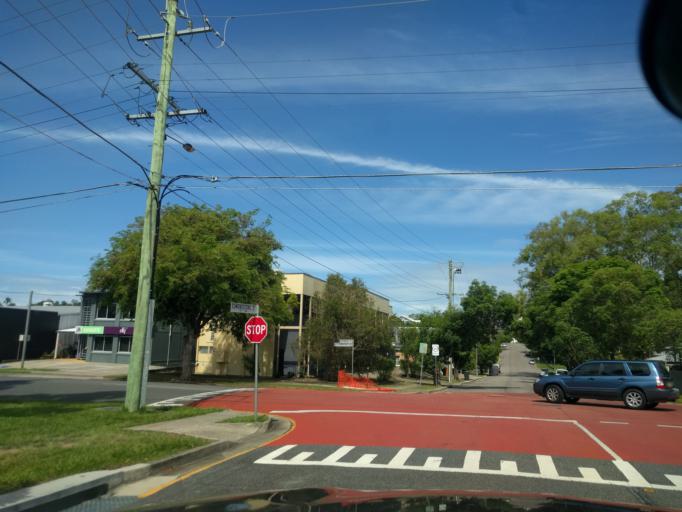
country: AU
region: Queensland
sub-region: Brisbane
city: Wilston
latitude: -27.4377
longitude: 153.0139
